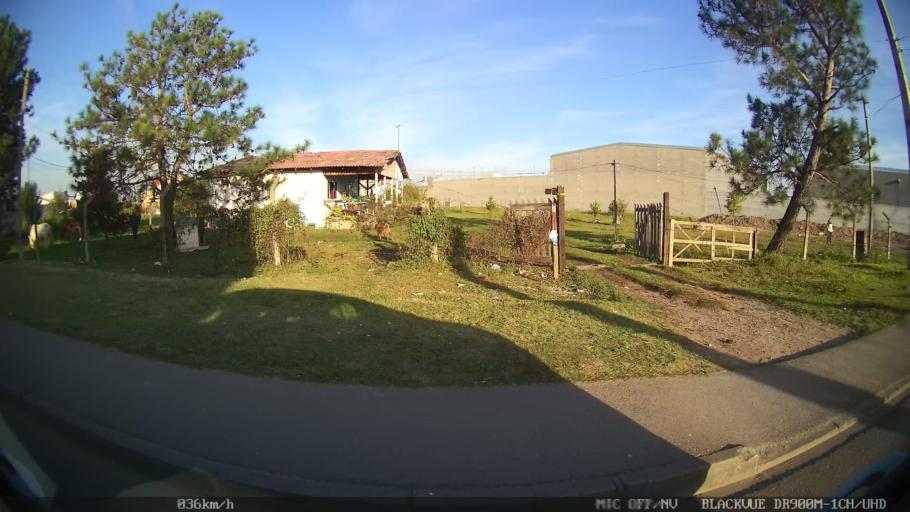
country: BR
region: Parana
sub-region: Pinhais
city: Pinhais
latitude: -25.4502
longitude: -49.1456
